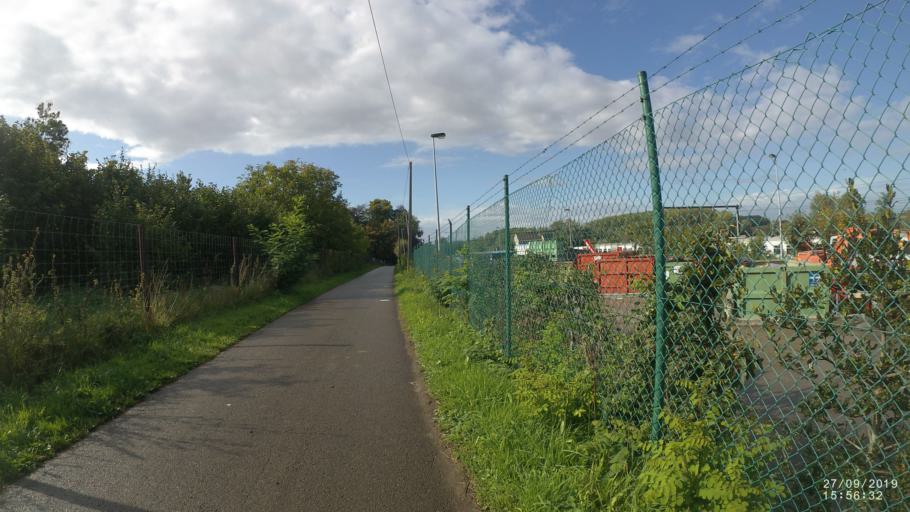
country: BE
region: Flanders
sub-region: Provincie Oost-Vlaanderen
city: Zottegem
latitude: 50.8688
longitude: 3.7571
